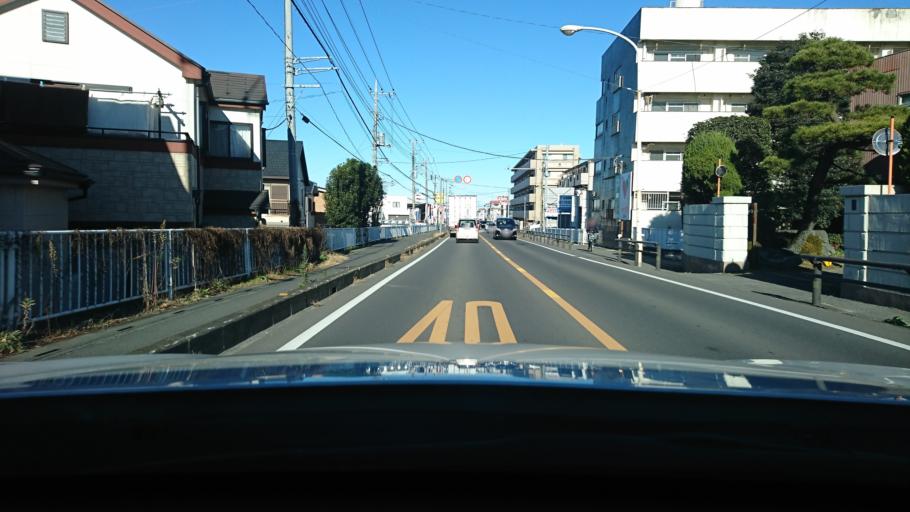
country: JP
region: Saitama
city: Kamifukuoka
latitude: 35.8729
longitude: 139.5032
